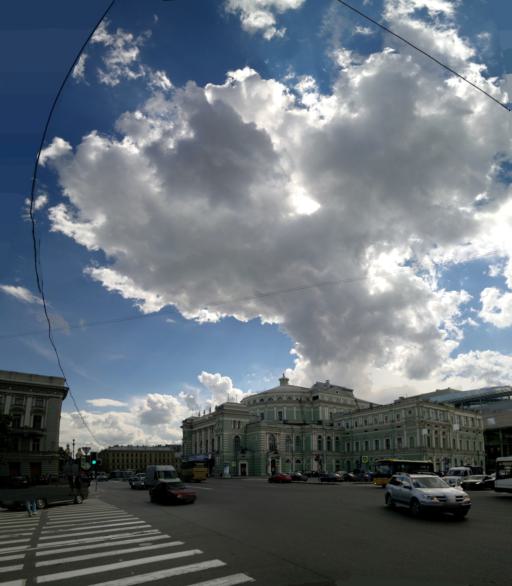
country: RU
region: St.-Petersburg
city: Saint Petersburg
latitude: 59.9269
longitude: 30.2966
